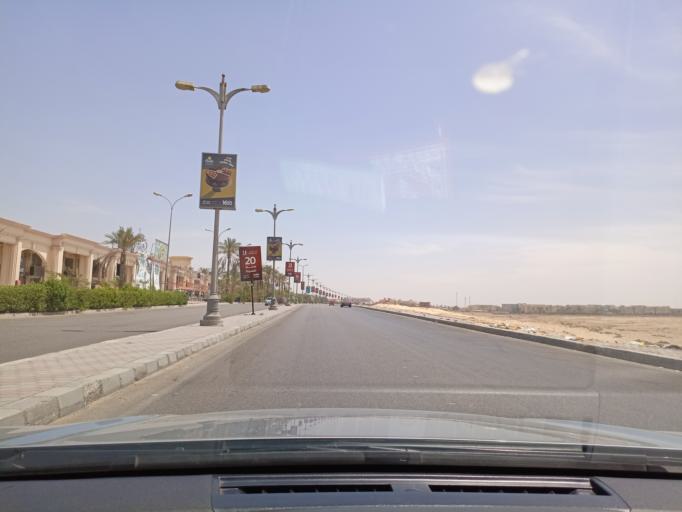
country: EG
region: Muhafazat al Qalyubiyah
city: Al Khankah
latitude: 30.1718
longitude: 31.4798
